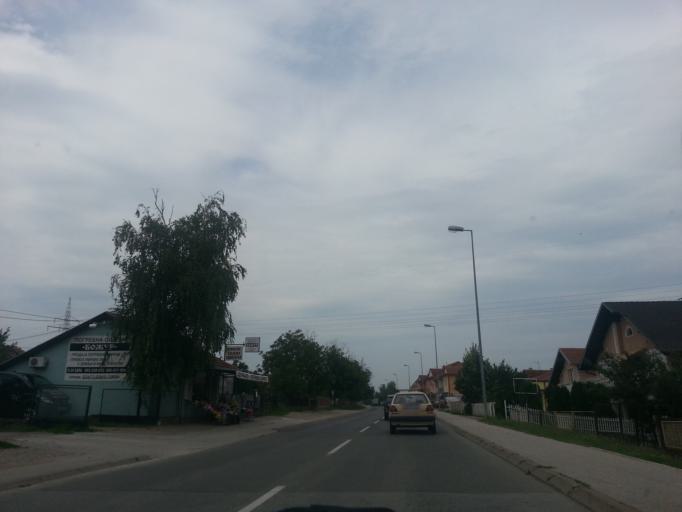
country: BA
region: Brcko
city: Brcko
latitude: 44.8542
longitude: 18.8142
